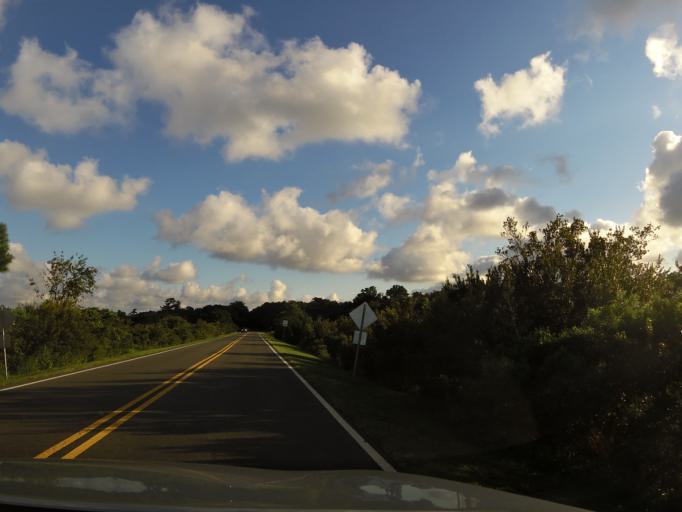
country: US
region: Georgia
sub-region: Glynn County
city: Saint Simon Mills
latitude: 31.1836
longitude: -81.3992
